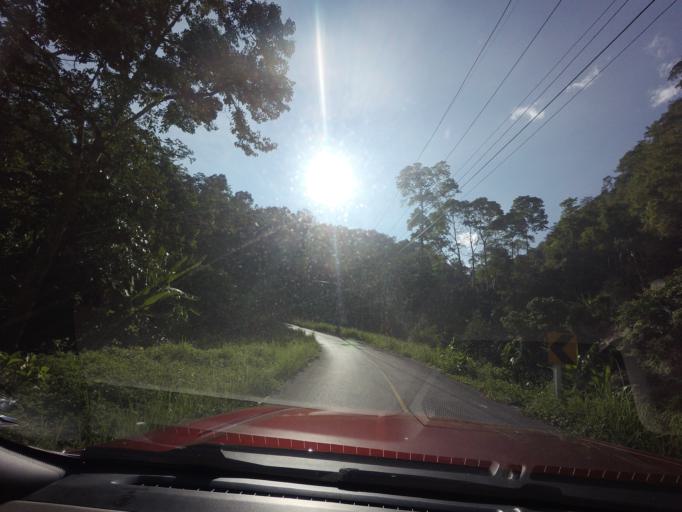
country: TH
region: Yala
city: Than To
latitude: 6.0879
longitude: 101.3277
